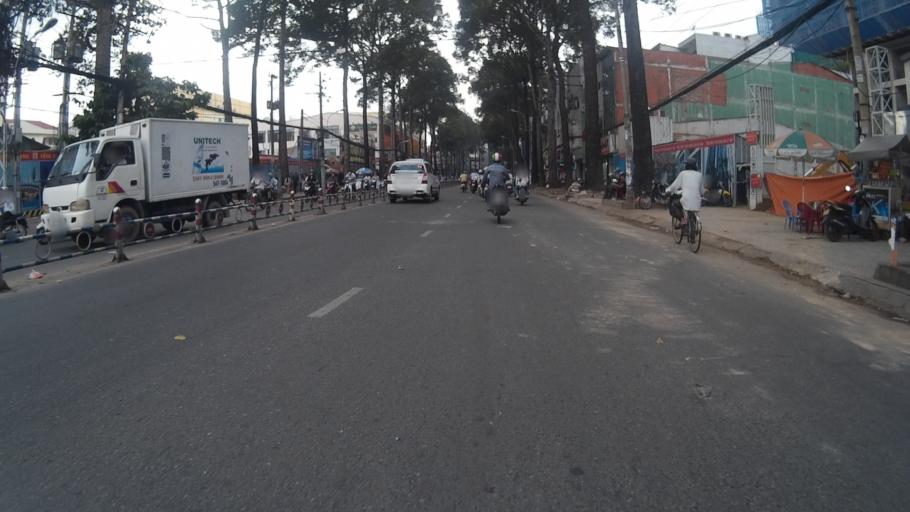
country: VN
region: Ho Chi Minh City
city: Quan Ba
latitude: 10.7773
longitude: 106.6811
